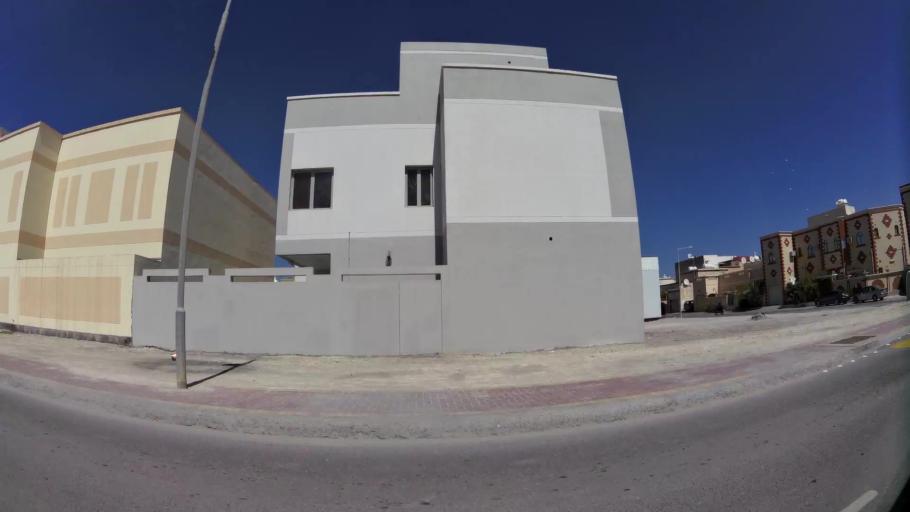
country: BH
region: Muharraq
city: Al Hadd
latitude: 26.2740
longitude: 50.6549
